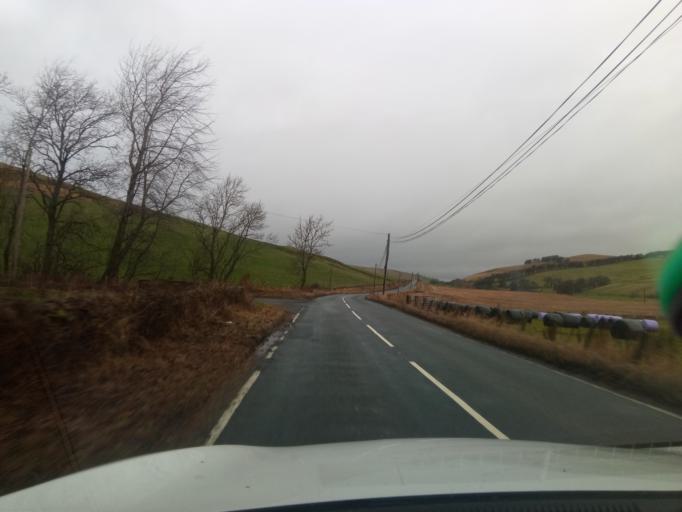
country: GB
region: Scotland
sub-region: The Scottish Borders
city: West Linton
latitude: 55.6640
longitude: -3.3182
